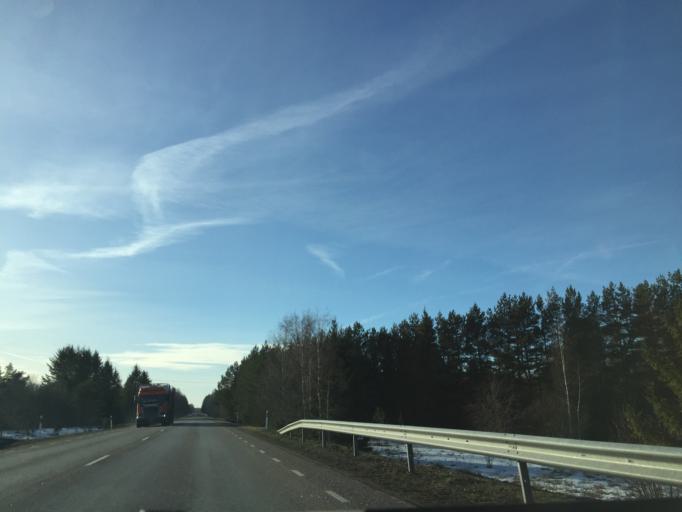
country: EE
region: Saare
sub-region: Orissaare vald
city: Orissaare
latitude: 58.5345
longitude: 23.0969
